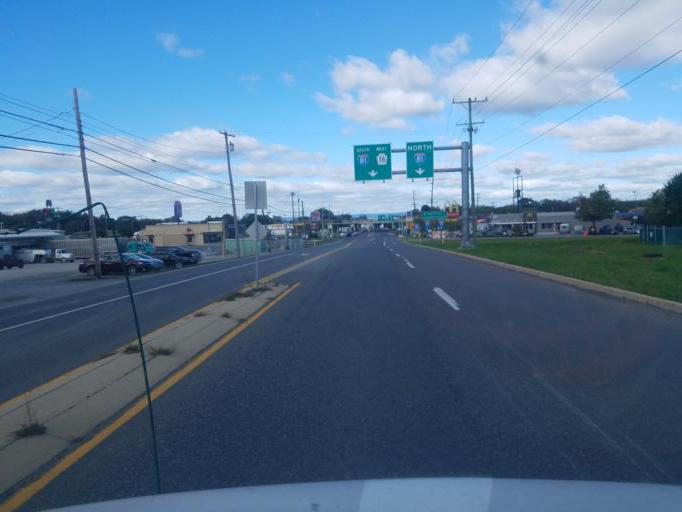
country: US
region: Pennsylvania
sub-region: Franklin County
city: Greencastle
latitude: 39.7859
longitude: -77.7096
